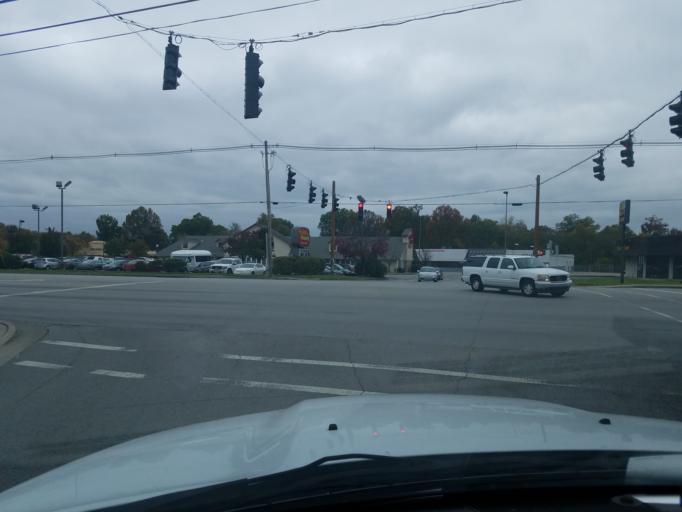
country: US
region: Kentucky
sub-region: Jefferson County
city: Pleasure Ridge Park
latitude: 38.1573
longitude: -85.8337
